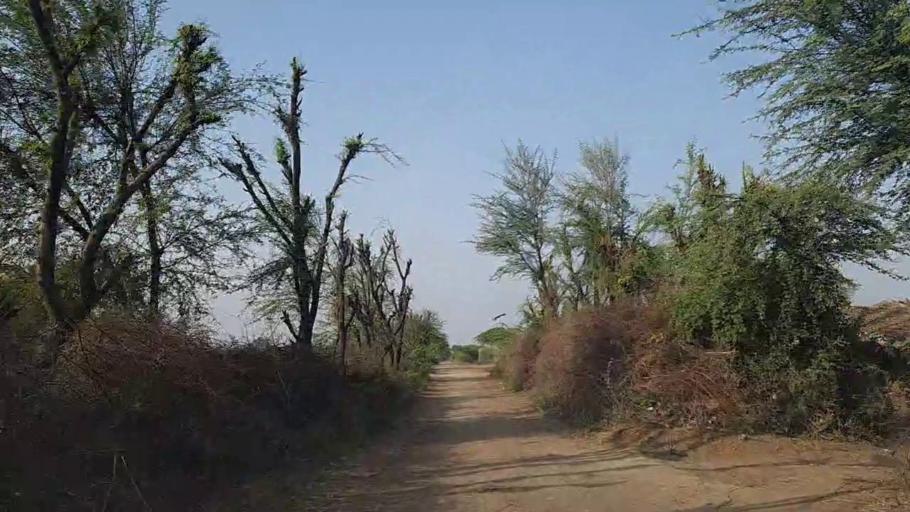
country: PK
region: Sindh
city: Dhoro Naro
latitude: 25.4961
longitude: 69.4998
